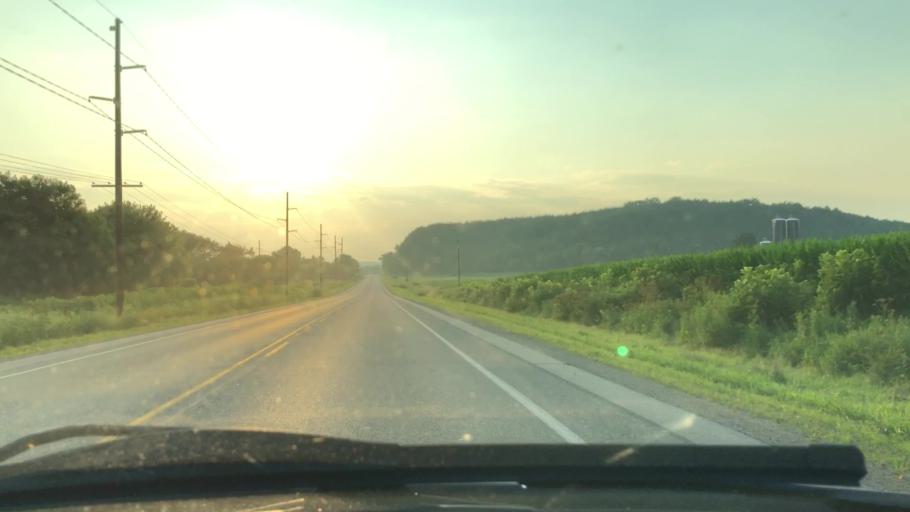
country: US
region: Wisconsin
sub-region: Dane County
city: Black Earth
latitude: 43.1319
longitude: -89.7241
